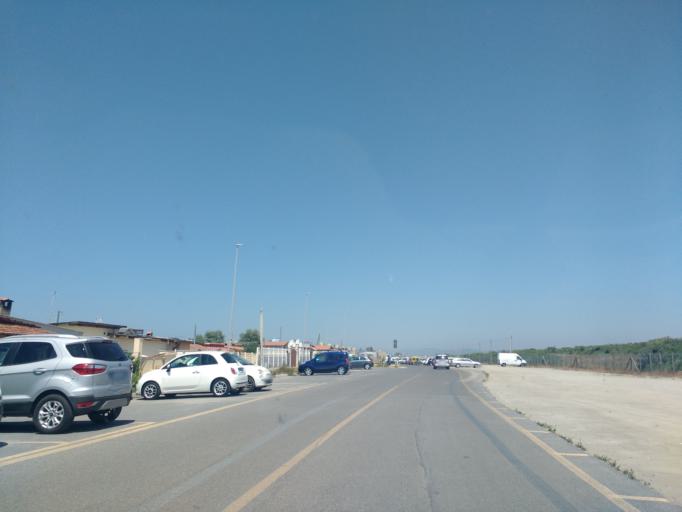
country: IT
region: Latium
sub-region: Citta metropolitana di Roma Capitale
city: Passo Oscuro
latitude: 41.8767
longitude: 12.1774
